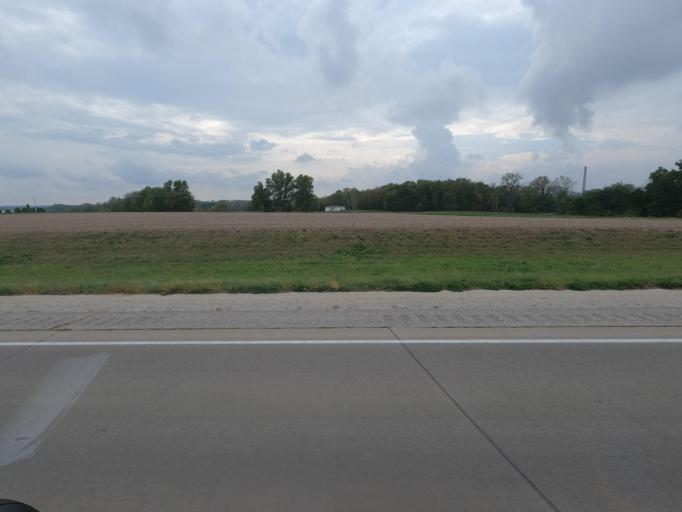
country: US
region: Iowa
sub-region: Wapello County
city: Eddyville
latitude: 41.1029
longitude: -92.5276
